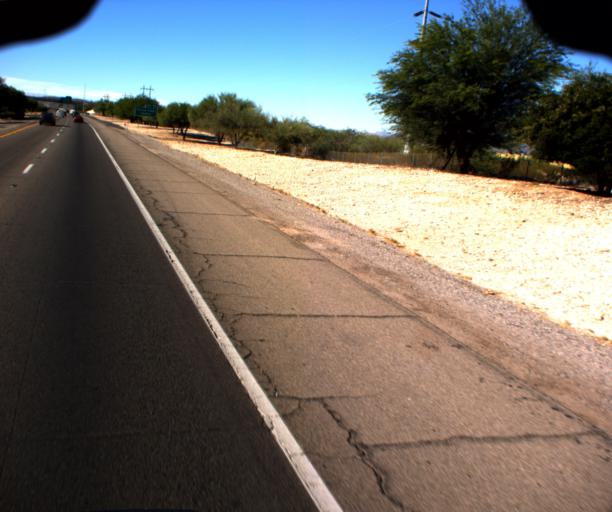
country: US
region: Arizona
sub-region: Pima County
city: Drexel Heights
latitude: 32.1521
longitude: -110.9868
